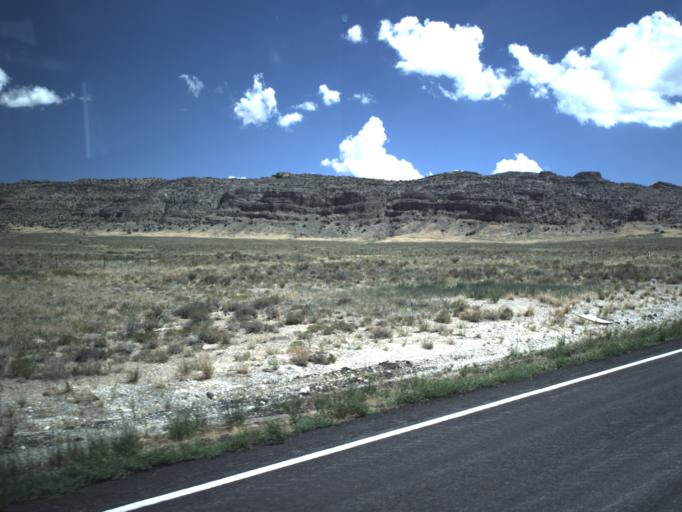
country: US
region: Utah
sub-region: Beaver County
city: Milford
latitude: 39.0762
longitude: -113.6827
